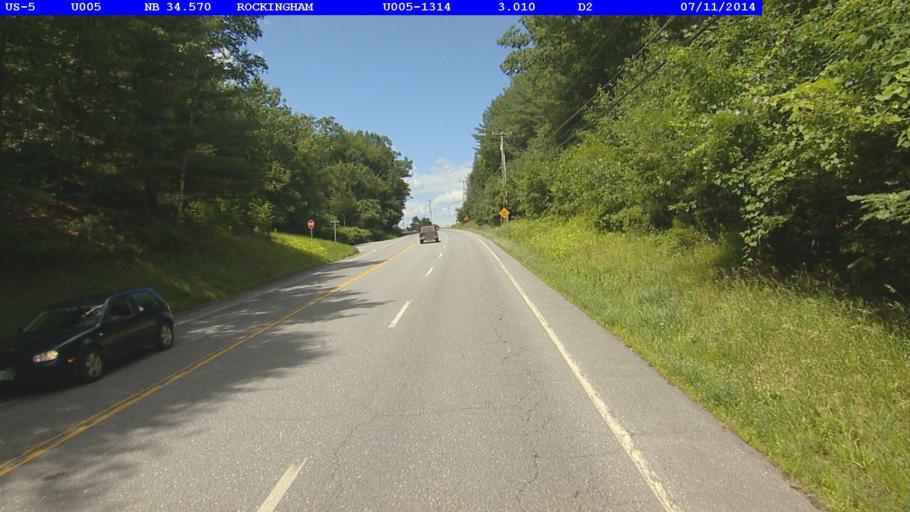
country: US
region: Vermont
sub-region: Windham County
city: Bellows Falls
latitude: 43.1644
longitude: -72.4566
